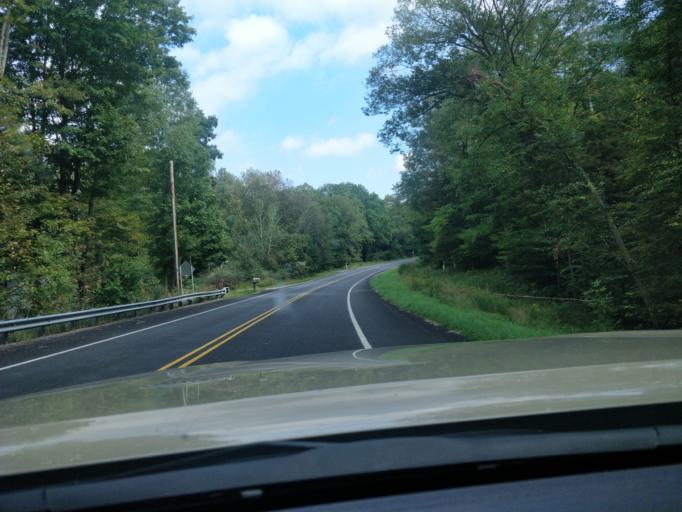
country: US
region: Michigan
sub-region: Ionia County
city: Saranac
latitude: 42.8874
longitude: -85.2100
